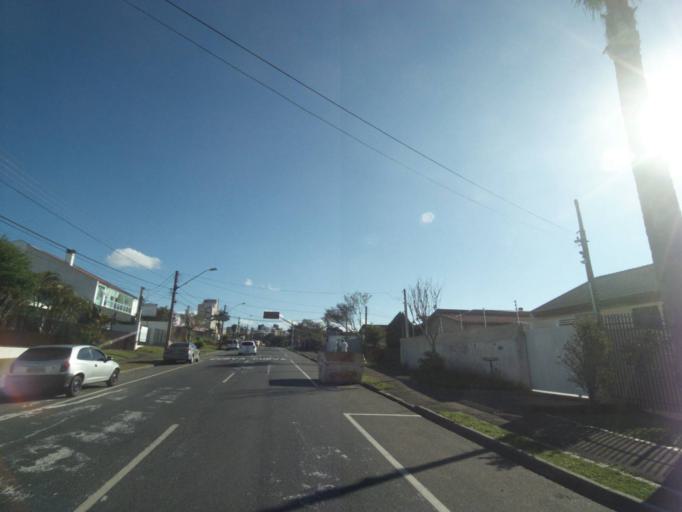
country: BR
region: Parana
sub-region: Curitiba
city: Curitiba
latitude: -25.3961
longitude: -49.2508
